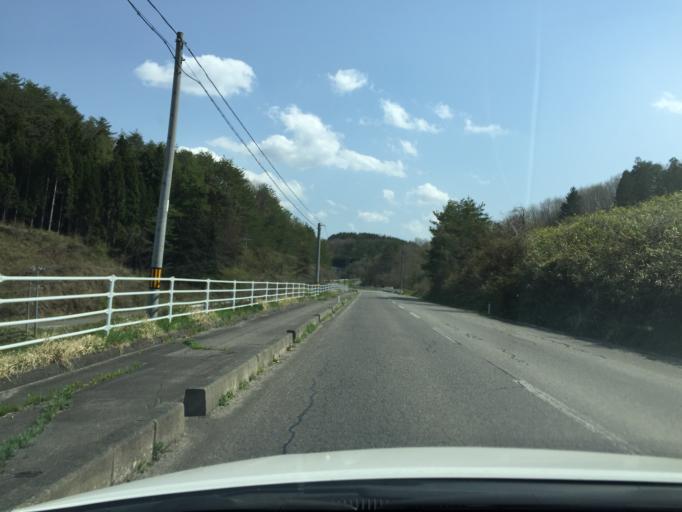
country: JP
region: Fukushima
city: Namie
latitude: 37.4030
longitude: 140.7996
